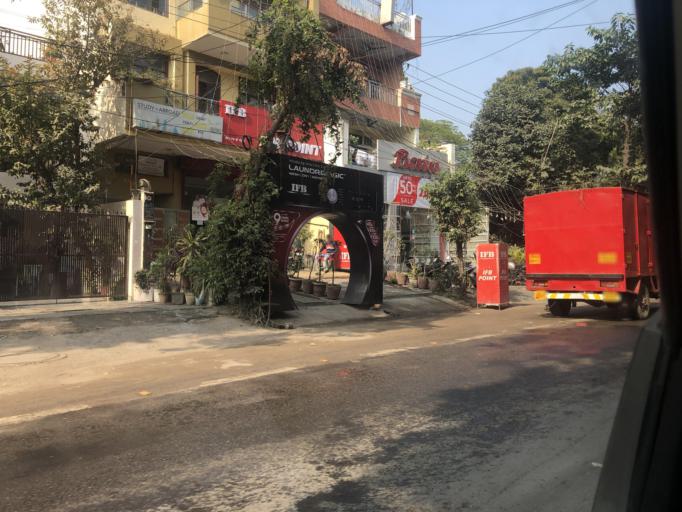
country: IN
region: Uttar Pradesh
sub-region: Gautam Buddha Nagar
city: Noida
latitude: 28.6472
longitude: 77.3597
